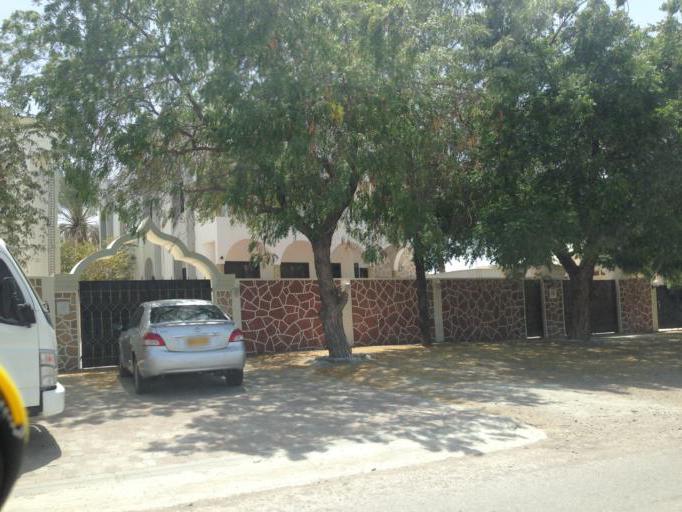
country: OM
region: Muhafazat Masqat
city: As Sib al Jadidah
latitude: 23.6823
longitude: 58.1215
